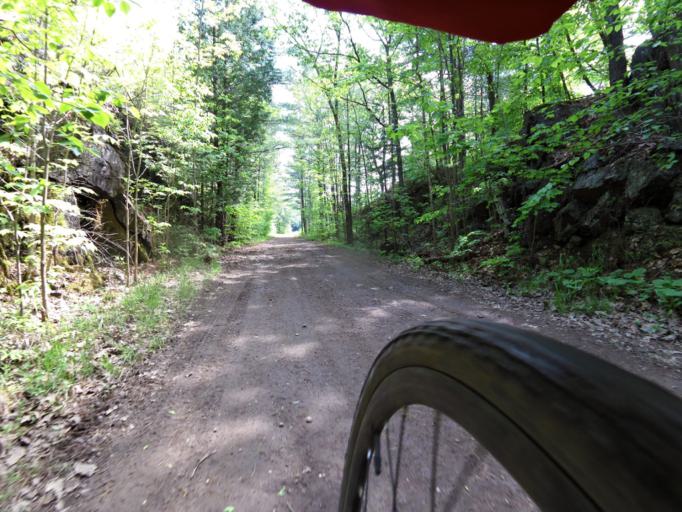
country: CA
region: Ontario
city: Renfrew
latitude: 45.2180
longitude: -76.6927
